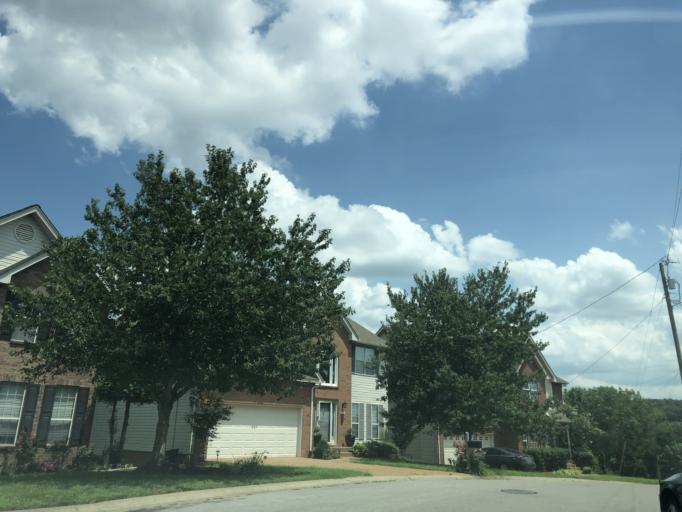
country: US
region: Tennessee
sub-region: Williamson County
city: Brentwood Estates
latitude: 36.0193
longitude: -86.7287
